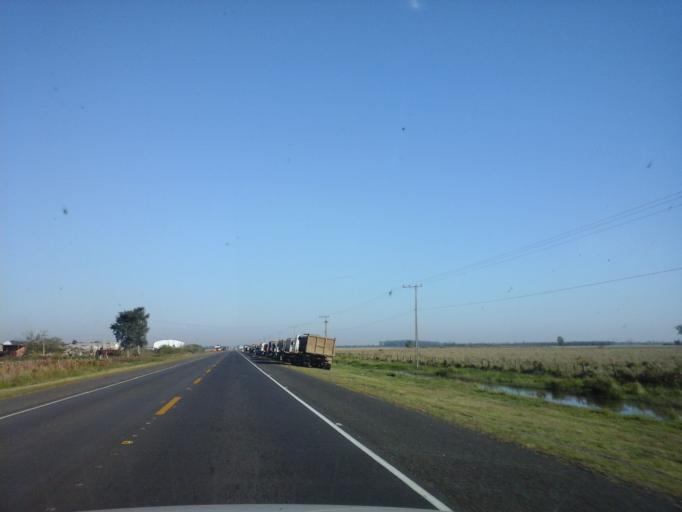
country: PY
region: Neembucu
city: Pilar
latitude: -26.8450
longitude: -58.2580
